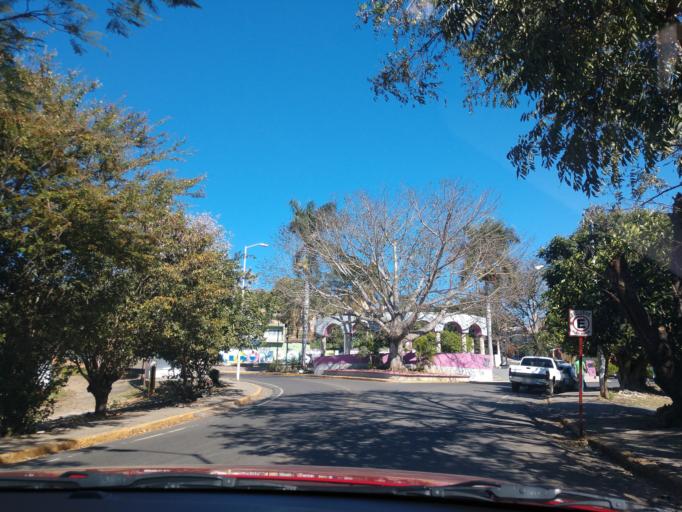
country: MX
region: Nayarit
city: Compostela
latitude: 21.2434
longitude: -104.9017
